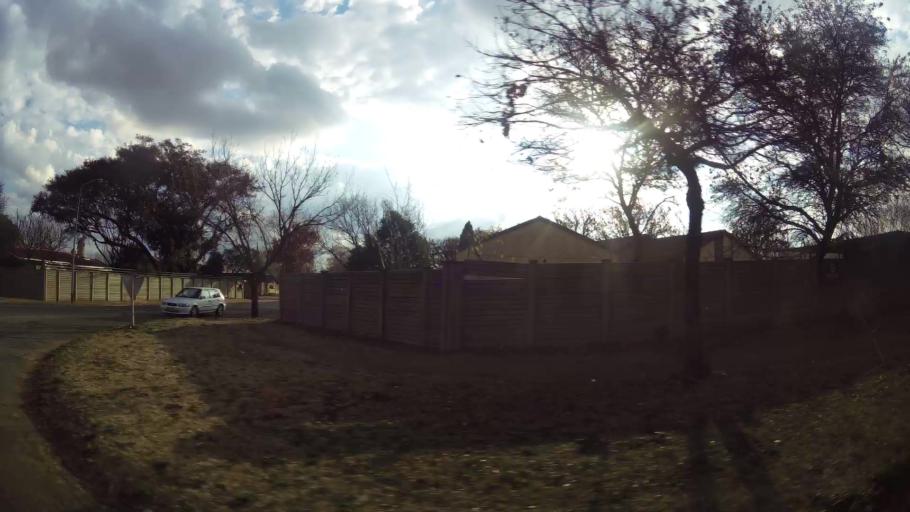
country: ZA
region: Orange Free State
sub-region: Fezile Dabi District Municipality
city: Sasolburg
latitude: -26.8191
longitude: 27.8088
